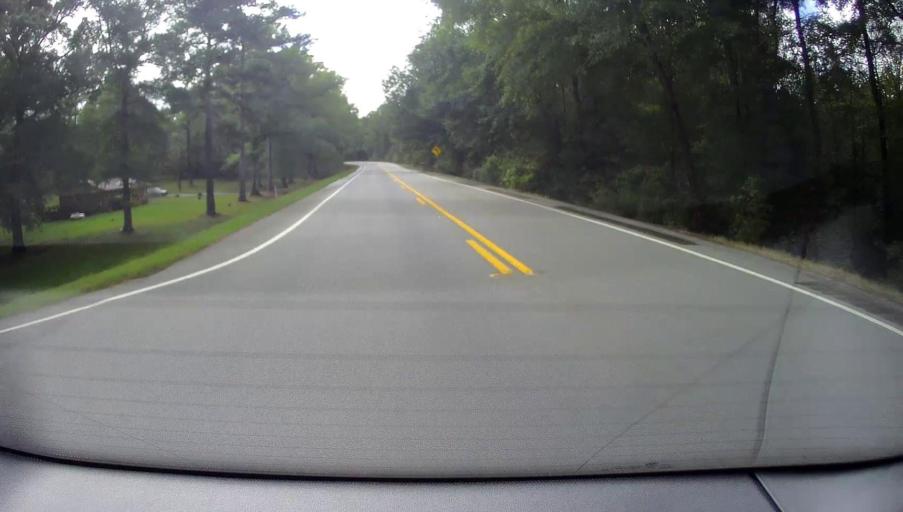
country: US
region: Georgia
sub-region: Baldwin County
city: Milledgeville
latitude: 33.0275
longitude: -83.3268
